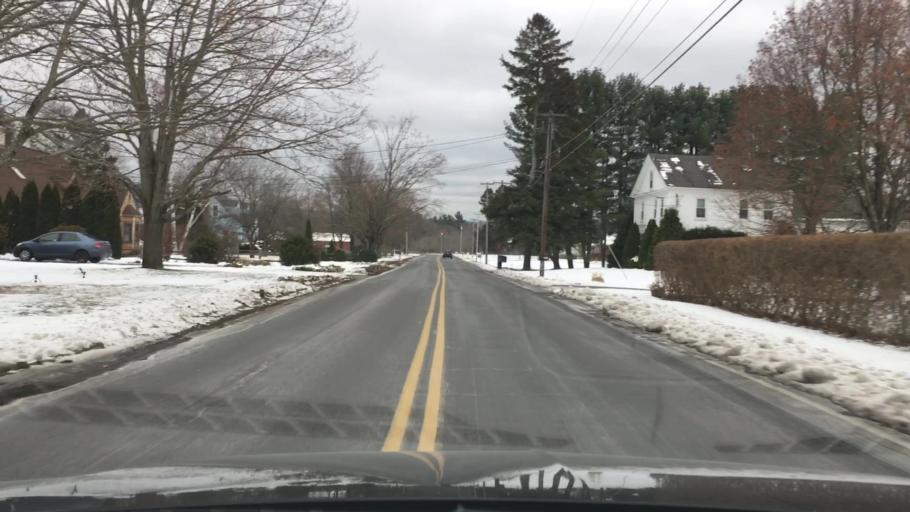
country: US
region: Connecticut
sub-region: Tolland County
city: Somers
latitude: 41.9968
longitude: -72.4695
